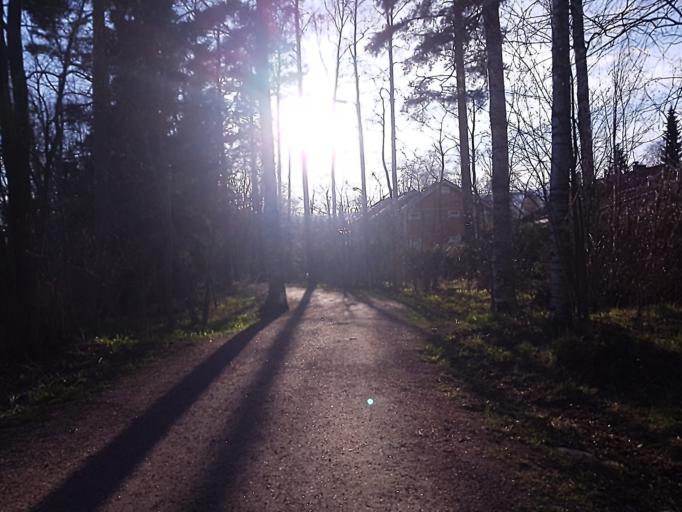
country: FI
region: Uusimaa
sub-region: Helsinki
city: Helsinki
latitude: 60.2531
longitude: 24.9247
